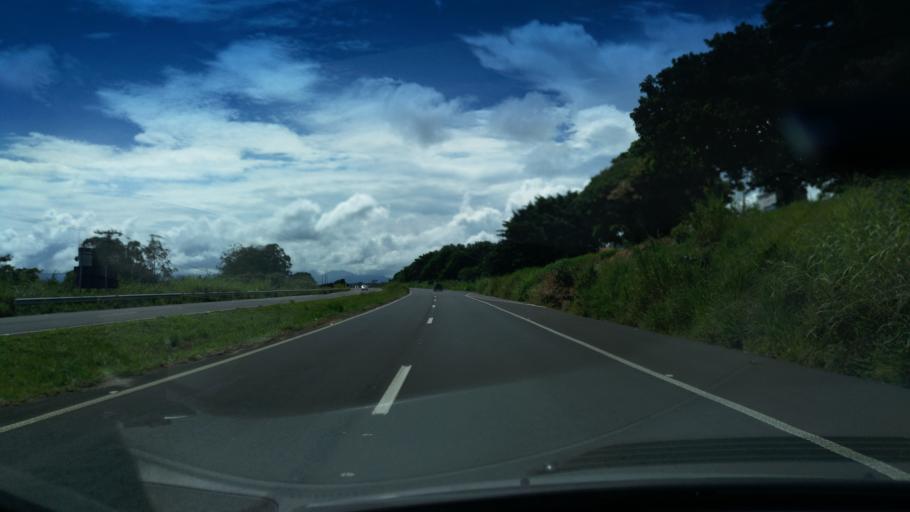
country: BR
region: Sao Paulo
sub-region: Santo Antonio Do Jardim
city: Espirito Santo do Pinhal
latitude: -22.1784
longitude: -46.7522
